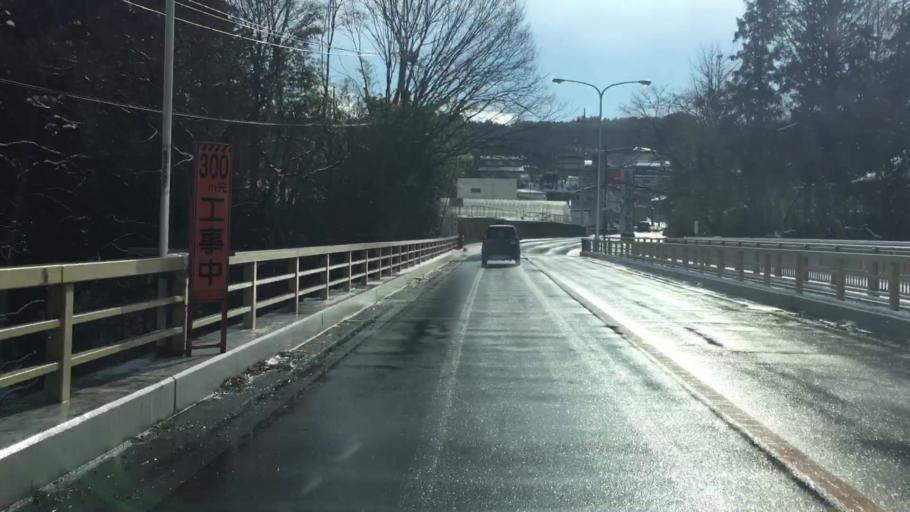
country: JP
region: Gunma
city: Numata
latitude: 36.6554
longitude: 139.0873
